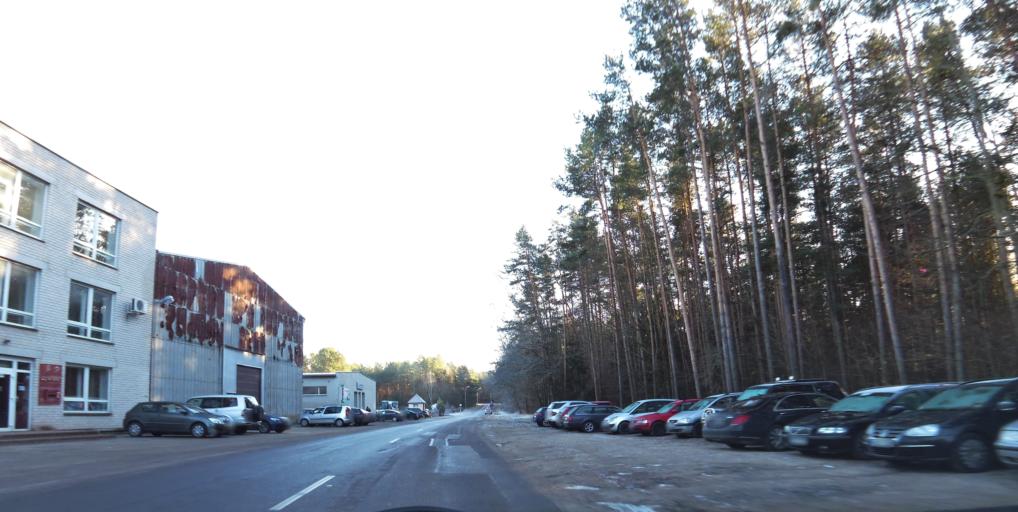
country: LT
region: Vilnius County
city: Lazdynai
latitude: 54.6419
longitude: 25.1748
